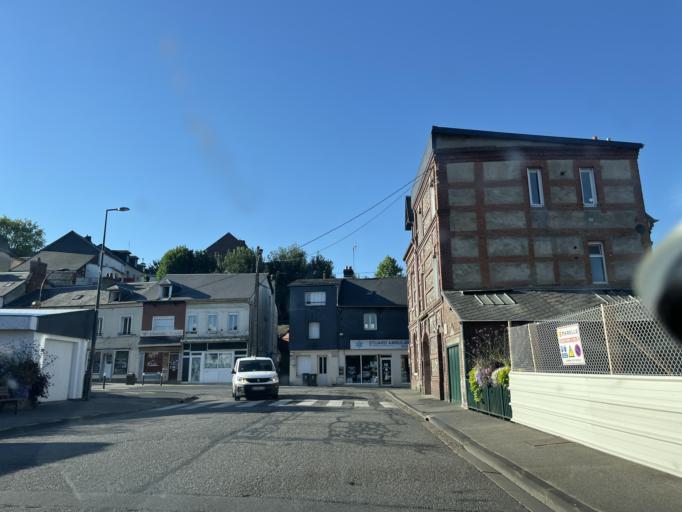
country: FR
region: Haute-Normandie
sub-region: Departement de la Seine-Maritime
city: Lillebonne
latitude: 49.5203
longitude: 0.5364
